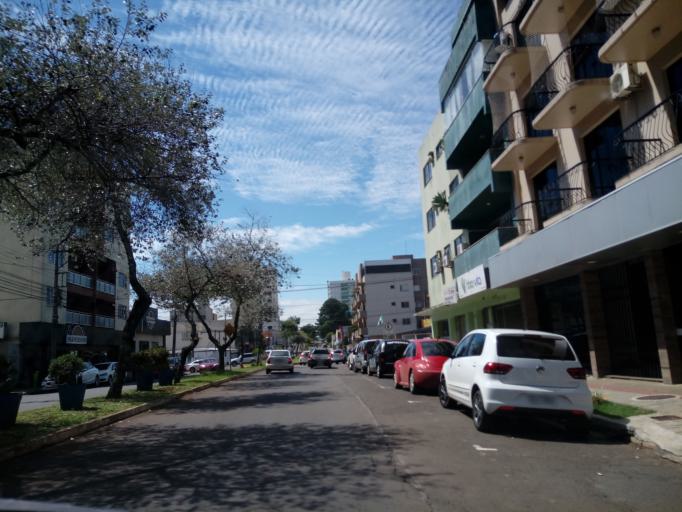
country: BR
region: Santa Catarina
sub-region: Chapeco
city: Chapeco
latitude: -27.0987
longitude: -52.6132
